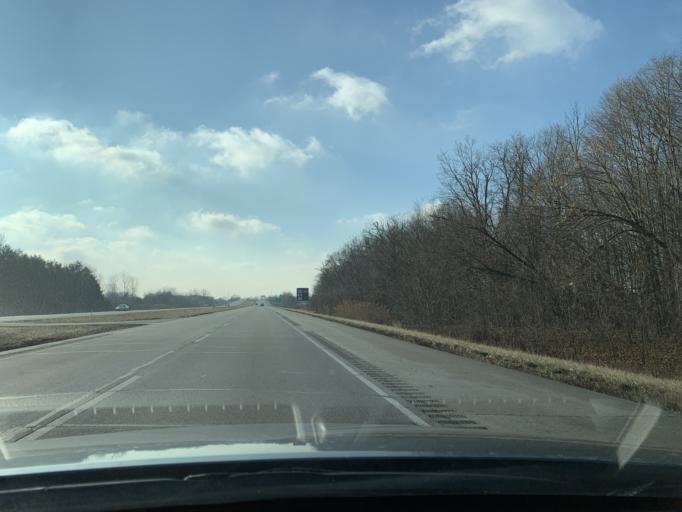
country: US
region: Indiana
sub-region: Porter County
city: Valparaiso
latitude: 41.4851
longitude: -87.0205
